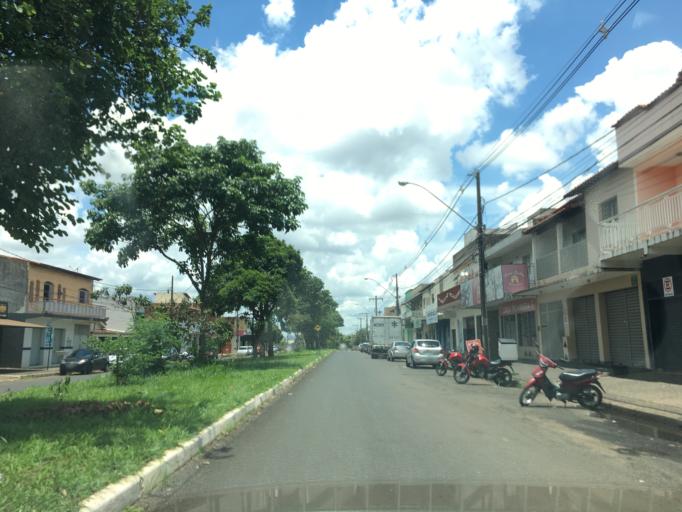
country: BR
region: Minas Gerais
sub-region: Uberlandia
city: Uberlandia
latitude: -18.9365
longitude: -48.3125
